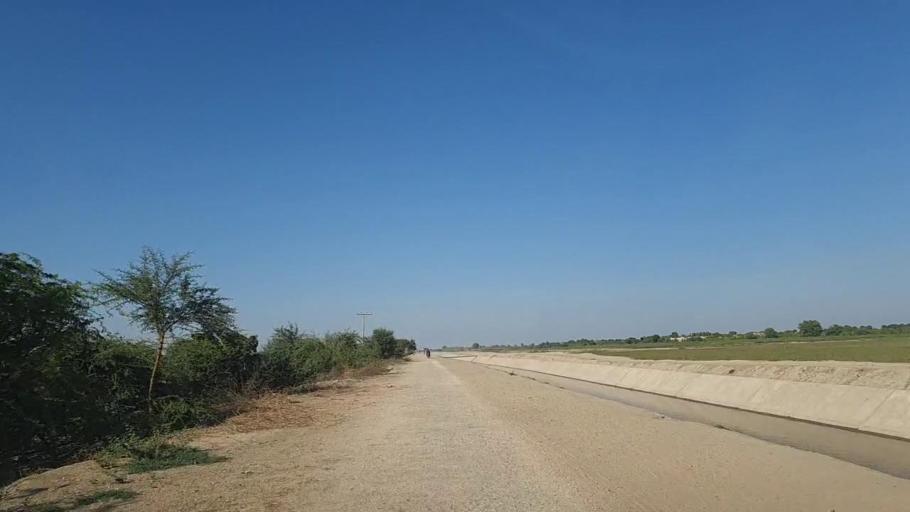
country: PK
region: Sindh
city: Kunri
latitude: 25.2316
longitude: 69.5153
